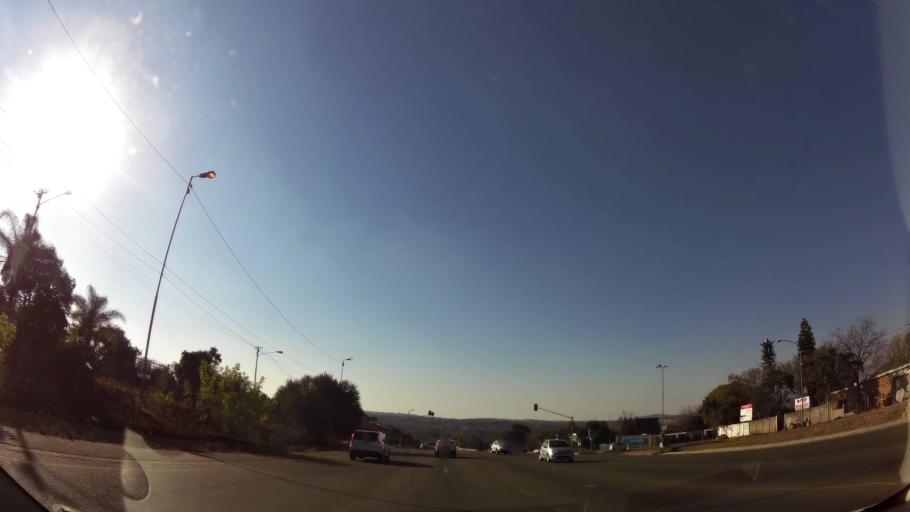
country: ZA
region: Gauteng
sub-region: City of Tshwane Metropolitan Municipality
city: Centurion
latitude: -25.8418
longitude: 28.1537
